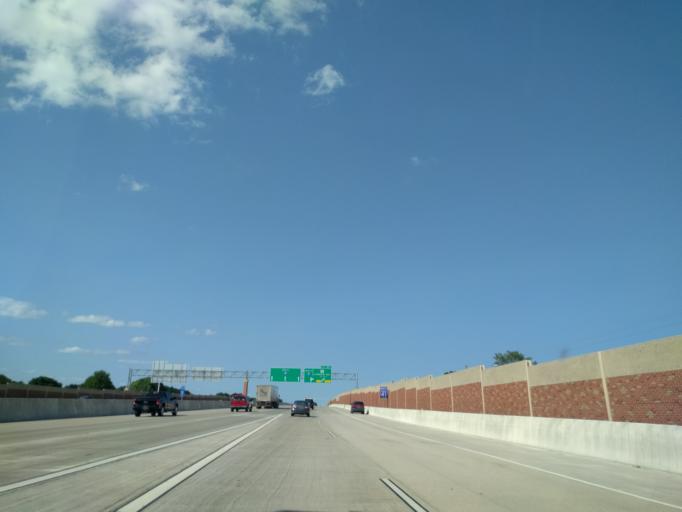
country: US
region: Wisconsin
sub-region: Brown County
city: Ashwaubenon
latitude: 44.4914
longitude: -88.0809
